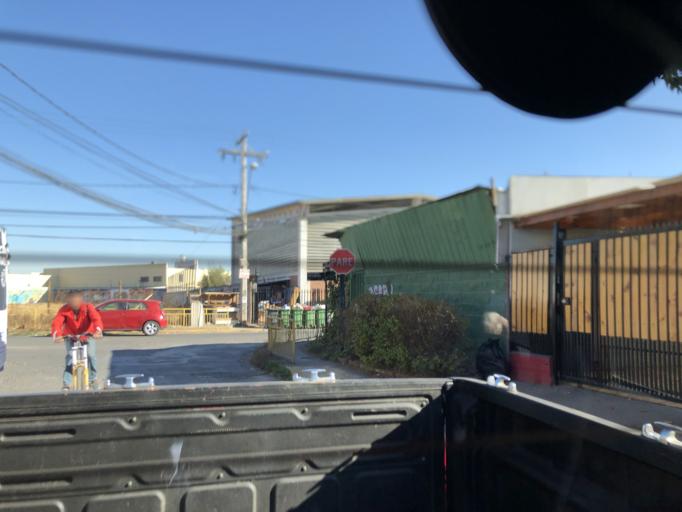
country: CL
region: Santiago Metropolitan
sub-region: Provincia de Cordillera
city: Puente Alto
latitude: -33.5933
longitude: -70.5576
